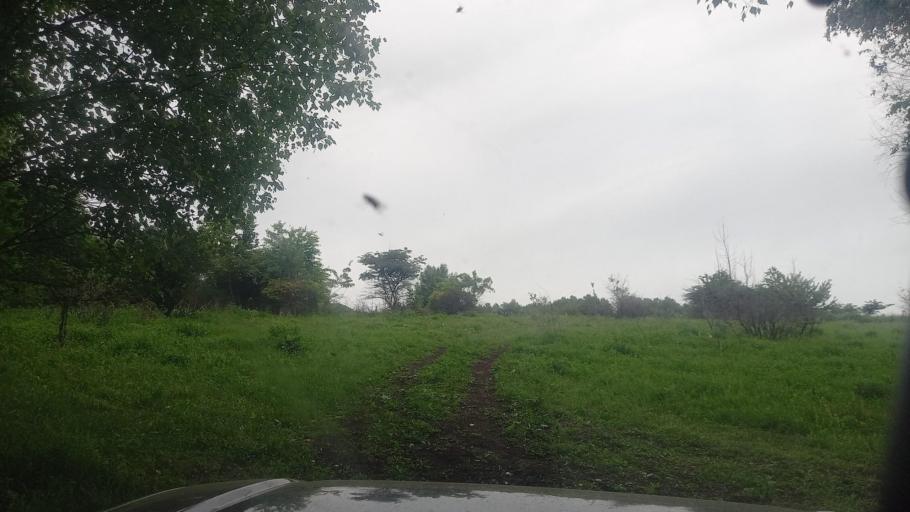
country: RU
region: Karachayevo-Cherkesiya
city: Pregradnaya
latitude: 44.0337
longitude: 41.3154
